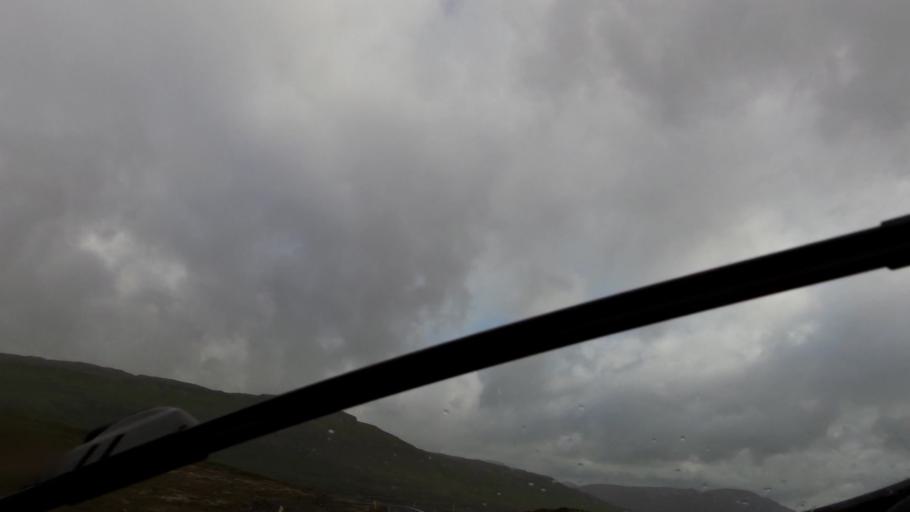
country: IS
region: Westfjords
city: Isafjoerdur
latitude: 65.5421
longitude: -23.1985
